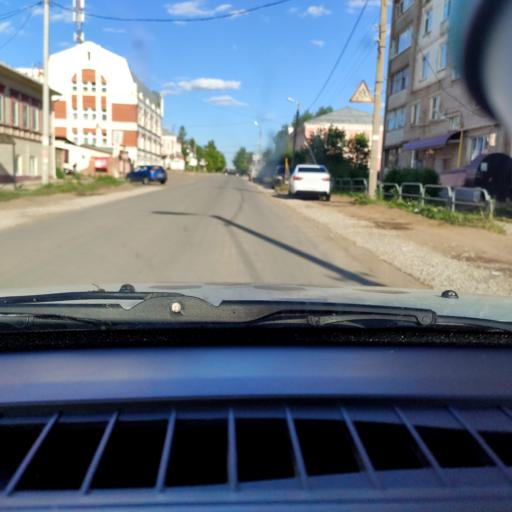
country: RU
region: Perm
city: Ocher
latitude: 57.8855
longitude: 54.7139
